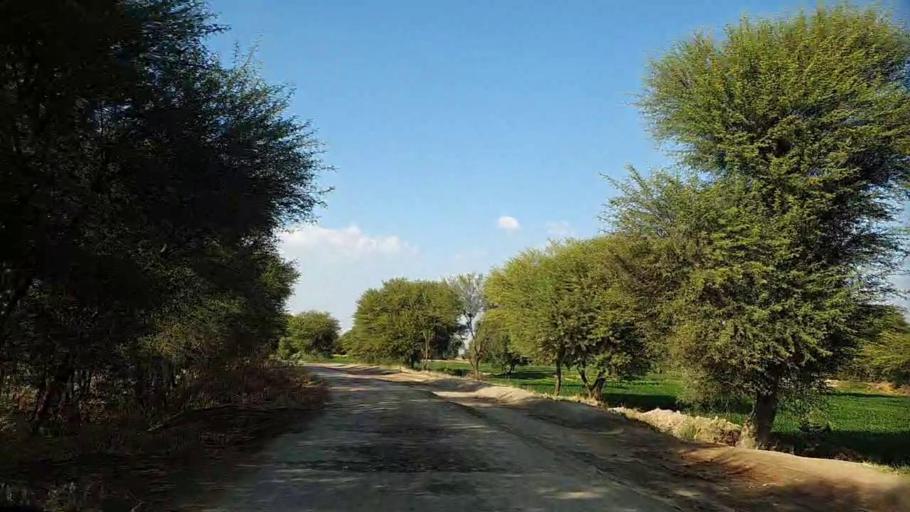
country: PK
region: Sindh
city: Pithoro
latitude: 25.6396
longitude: 69.3509
